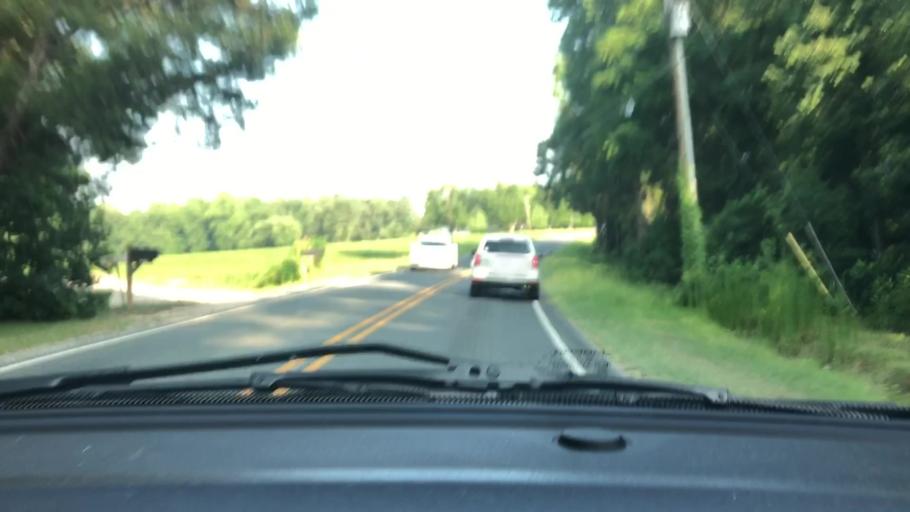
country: US
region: North Carolina
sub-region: Lee County
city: Broadway
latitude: 35.3567
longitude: -79.0793
